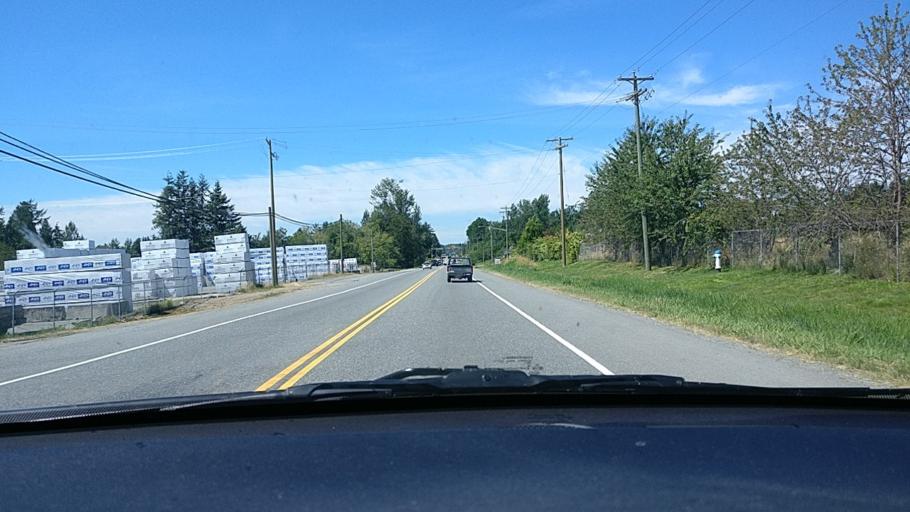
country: CA
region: British Columbia
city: Aldergrove
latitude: 49.0570
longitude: -122.4306
